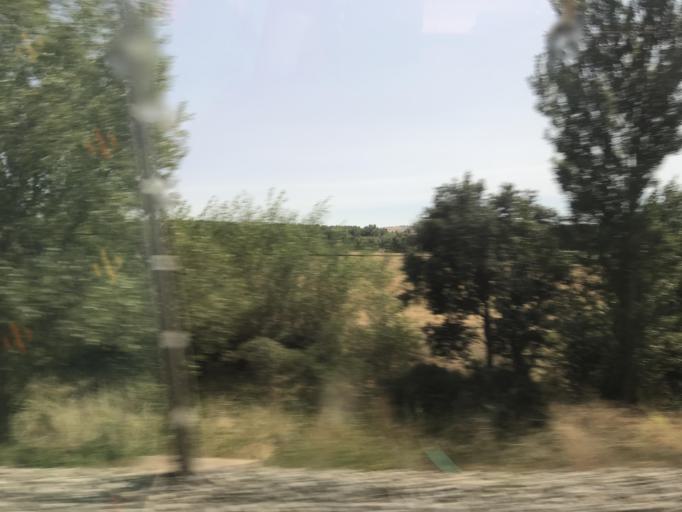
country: ES
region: Castille and Leon
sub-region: Provincia de Burgos
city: Villaverde-Mogina
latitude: 42.1695
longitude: -4.0670
